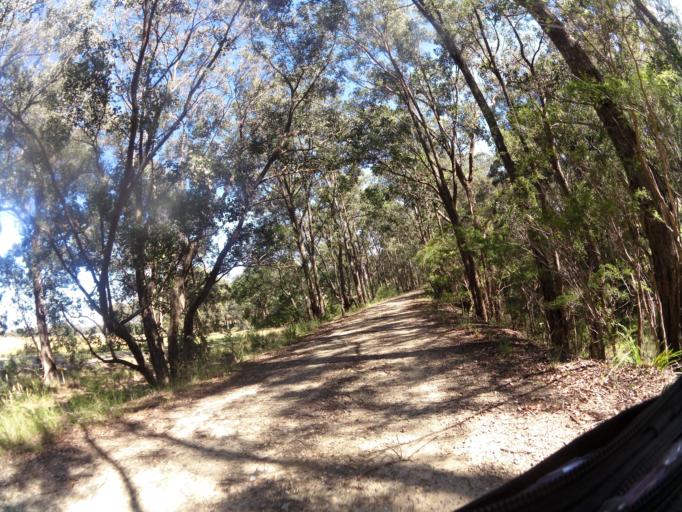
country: AU
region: Victoria
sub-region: East Gippsland
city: Lakes Entrance
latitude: -37.7412
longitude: 148.1695
